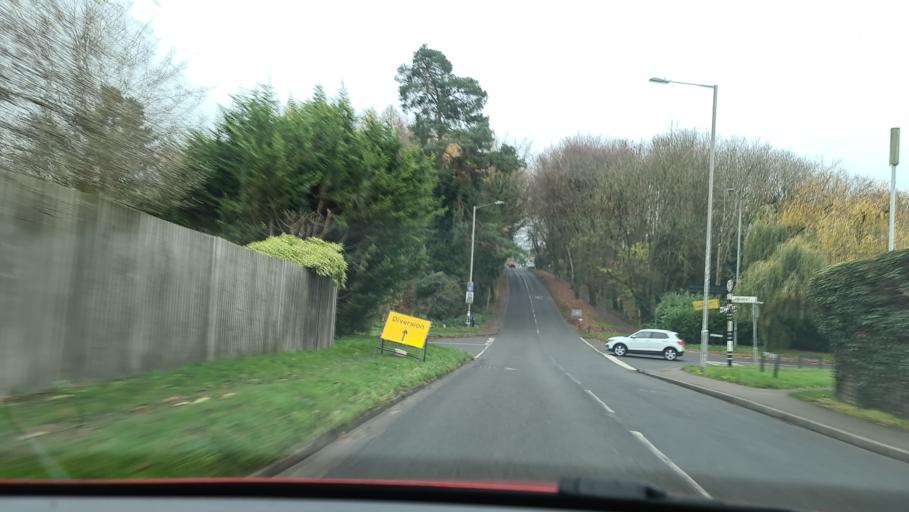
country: GB
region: England
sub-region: Buckinghamshire
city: Beaconsfield
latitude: 51.6400
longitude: -0.6932
